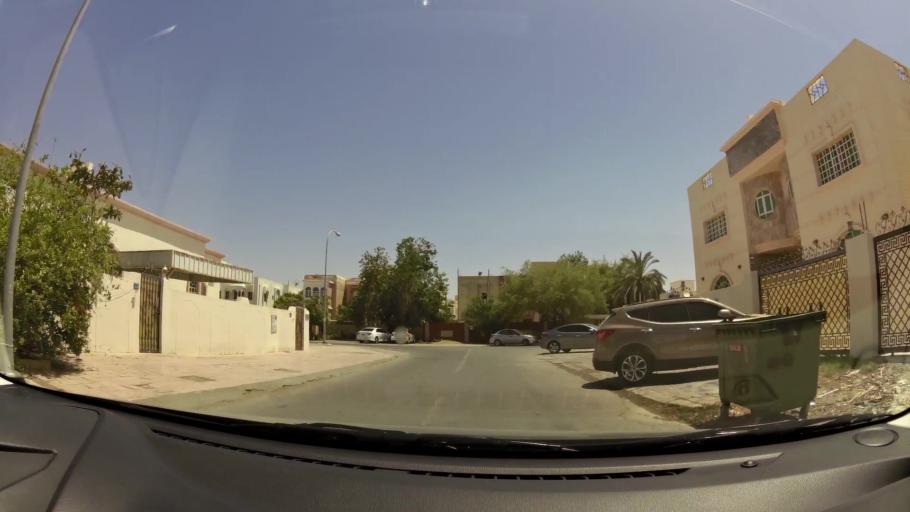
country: OM
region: Muhafazat Masqat
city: Bawshar
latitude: 23.5984
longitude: 58.3774
